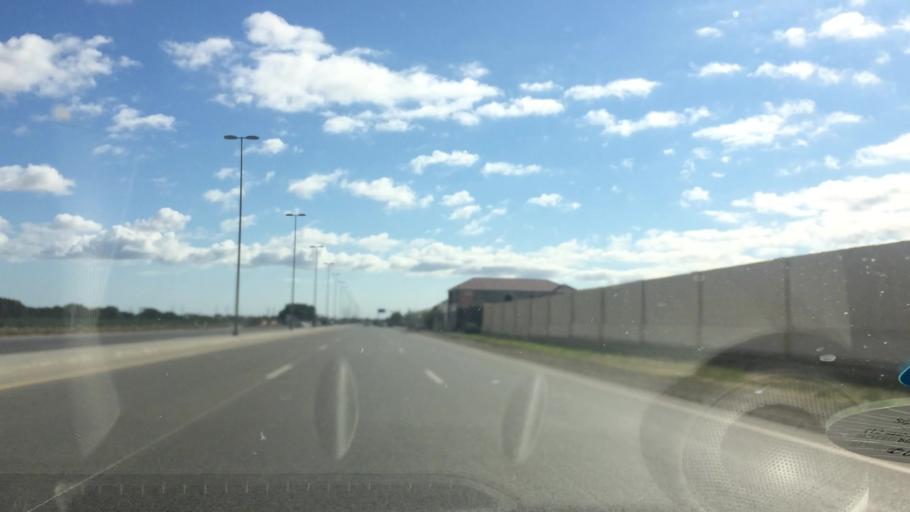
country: AZ
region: Baki
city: Qala
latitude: 40.4473
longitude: 50.1664
